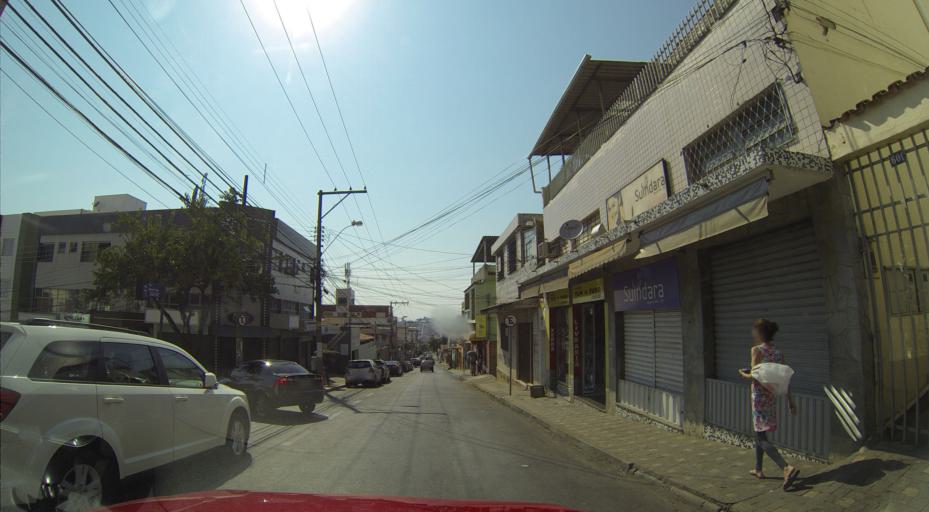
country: BR
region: Minas Gerais
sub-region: Belo Horizonte
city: Belo Horizonte
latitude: -19.9064
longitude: -43.9702
